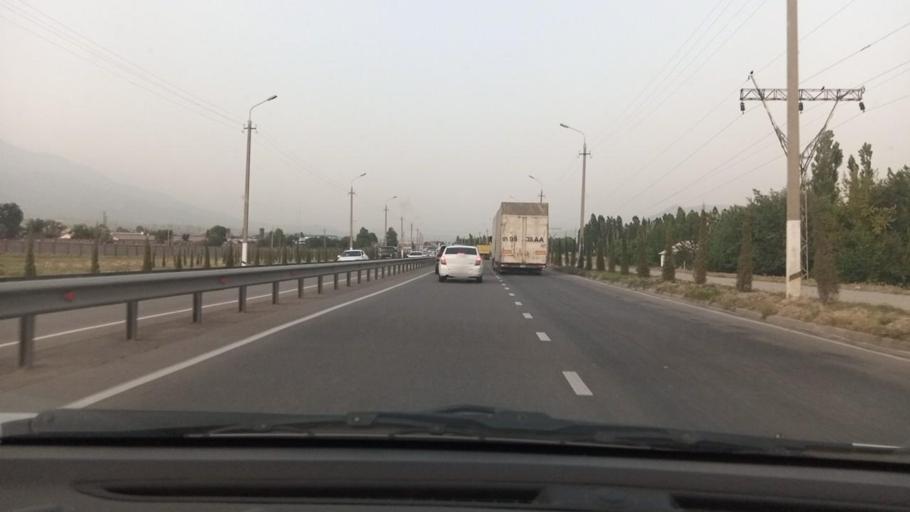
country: UZ
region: Toshkent
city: Angren
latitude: 41.0231
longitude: 70.1287
